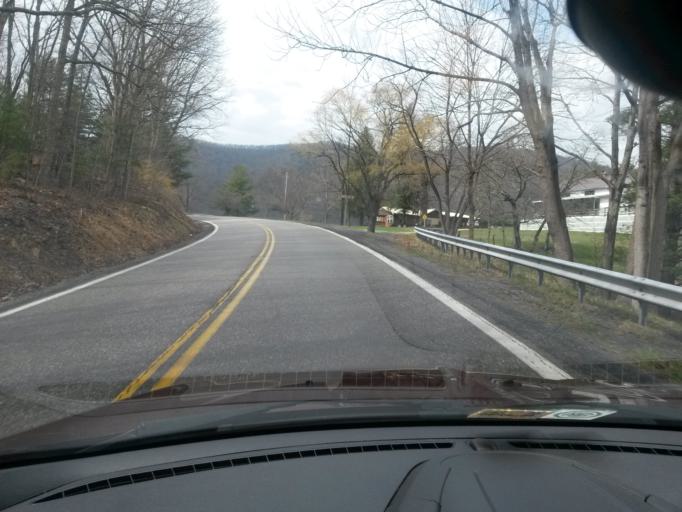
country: US
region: Virginia
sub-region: Bath County
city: Warm Springs
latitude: 38.0495
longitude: -79.7510
